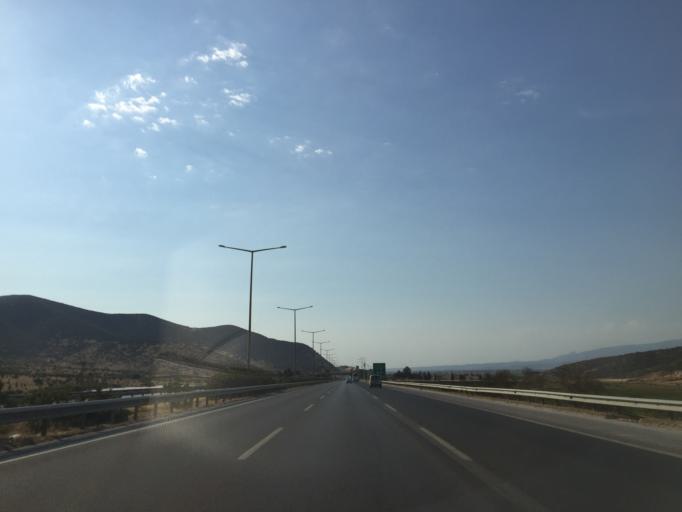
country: TR
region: Izmir
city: Belevi
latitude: 38.0630
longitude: 27.4182
